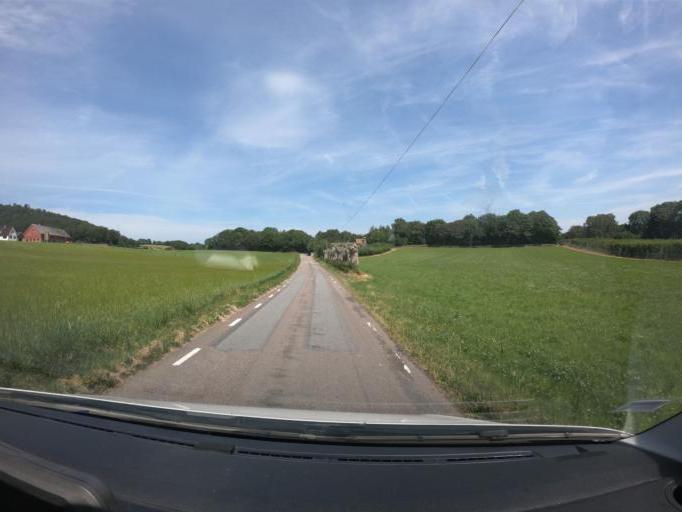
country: SE
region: Skane
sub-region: Bastads Kommun
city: Bastad
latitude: 56.4566
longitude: 12.7525
